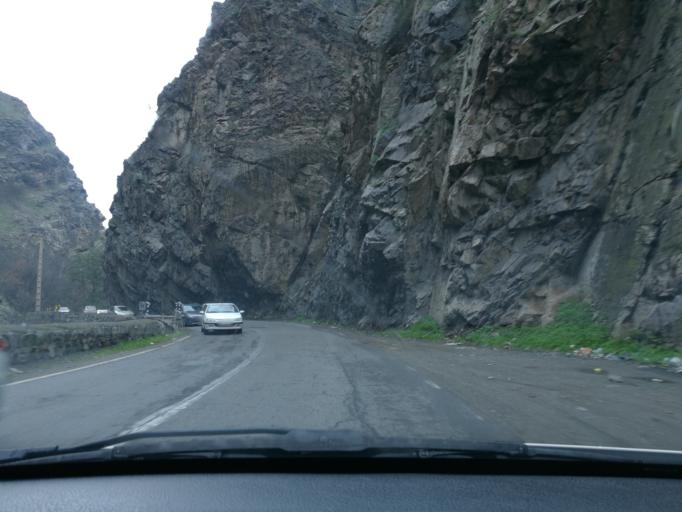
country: IR
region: Mazandaran
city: Chalus
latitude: 36.2961
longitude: 51.2461
